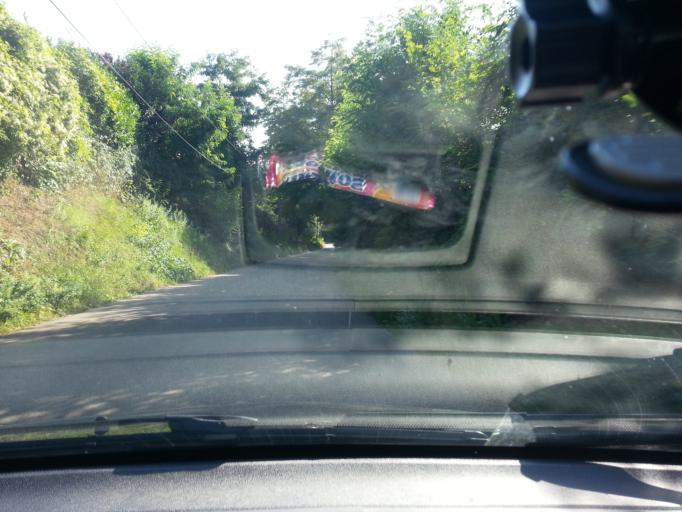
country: FR
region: Bourgogne
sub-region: Departement de Saone-et-Loire
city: Saint-Remy
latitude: 46.7643
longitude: 4.8160
